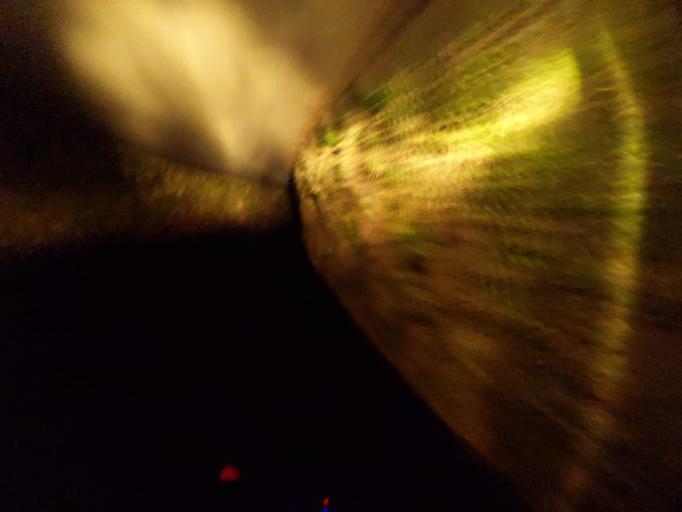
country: GB
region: England
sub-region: Cornwall
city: Torpoint
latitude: 50.3483
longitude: -4.2268
